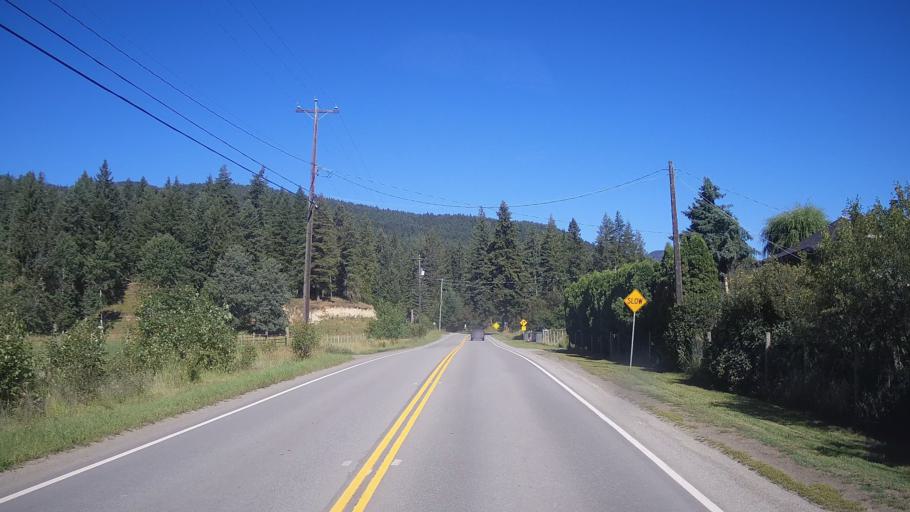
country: CA
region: British Columbia
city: Kamloops
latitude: 51.4257
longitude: -120.2095
